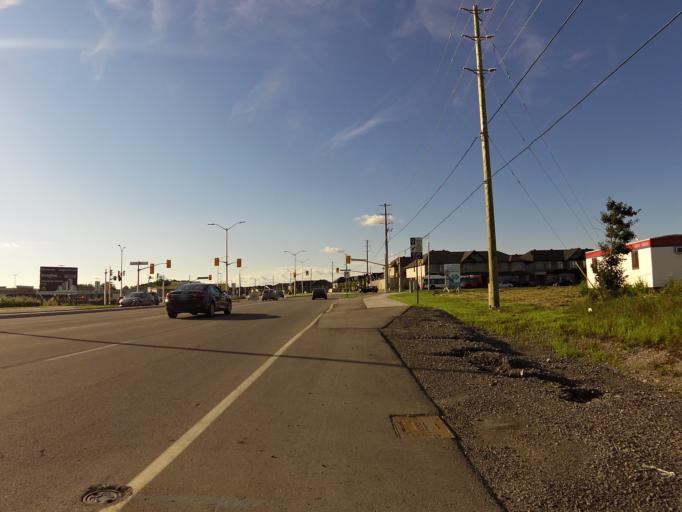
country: CA
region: Ontario
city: Bells Corners
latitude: 45.2682
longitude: -75.7795
